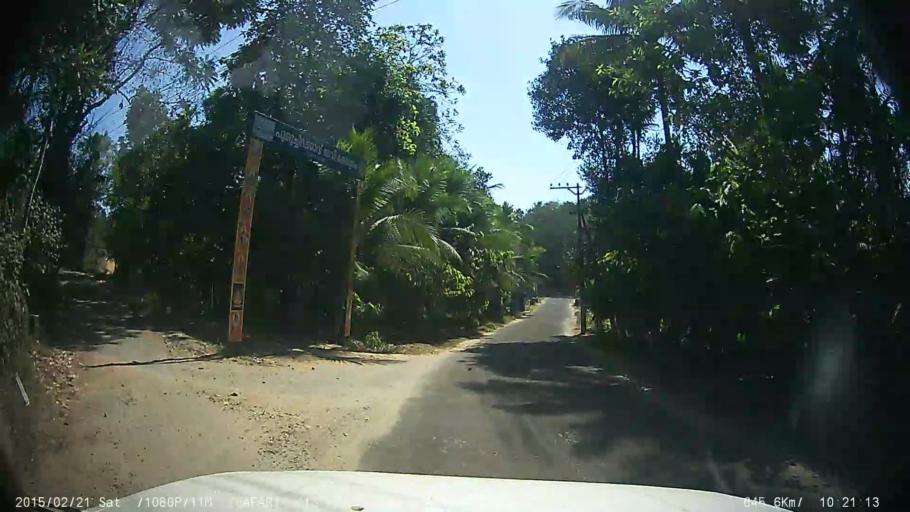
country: IN
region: Kerala
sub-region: Kottayam
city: Palackattumala
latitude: 9.8689
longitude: 76.6670
